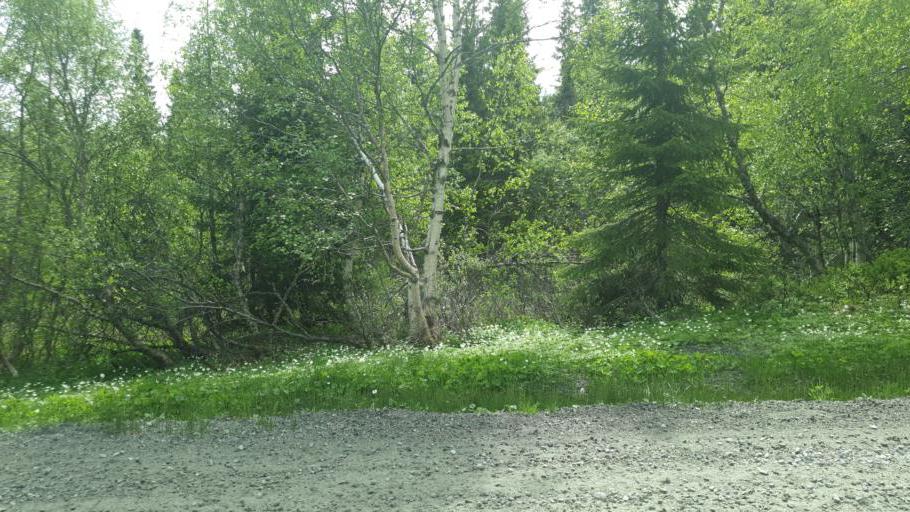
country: NO
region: Nord-Trondelag
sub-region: Leksvik
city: Leksvik
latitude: 63.6969
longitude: 10.4802
